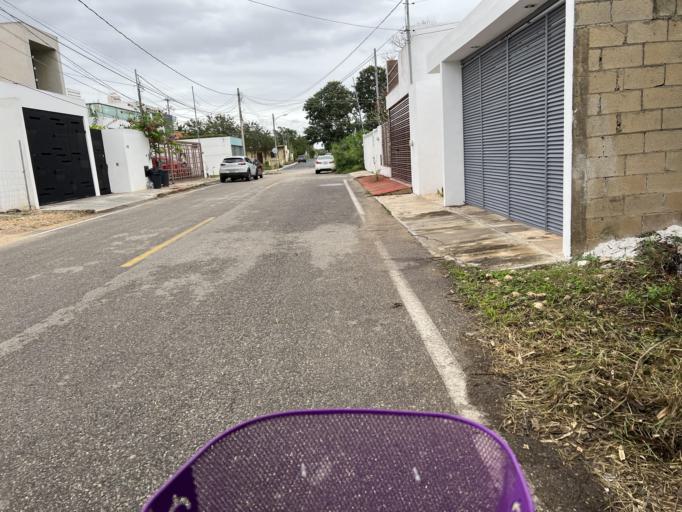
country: MX
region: Yucatan
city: Merida
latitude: 20.9980
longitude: -89.5843
